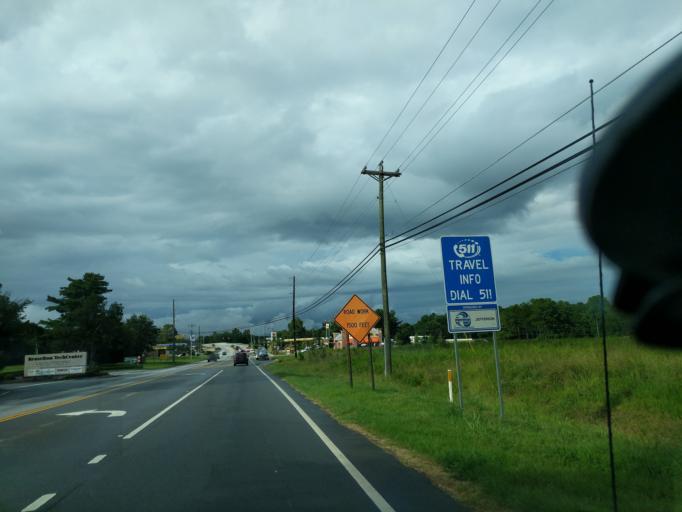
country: US
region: Georgia
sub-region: Jackson County
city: Braselton
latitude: 34.1135
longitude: -83.7632
